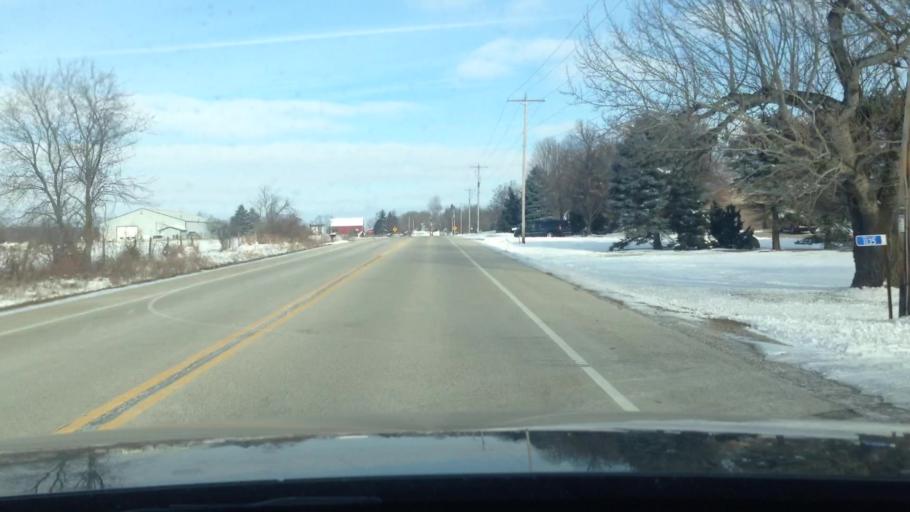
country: US
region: Wisconsin
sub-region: Walworth County
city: Lake Geneva
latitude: 42.6643
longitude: -88.4138
